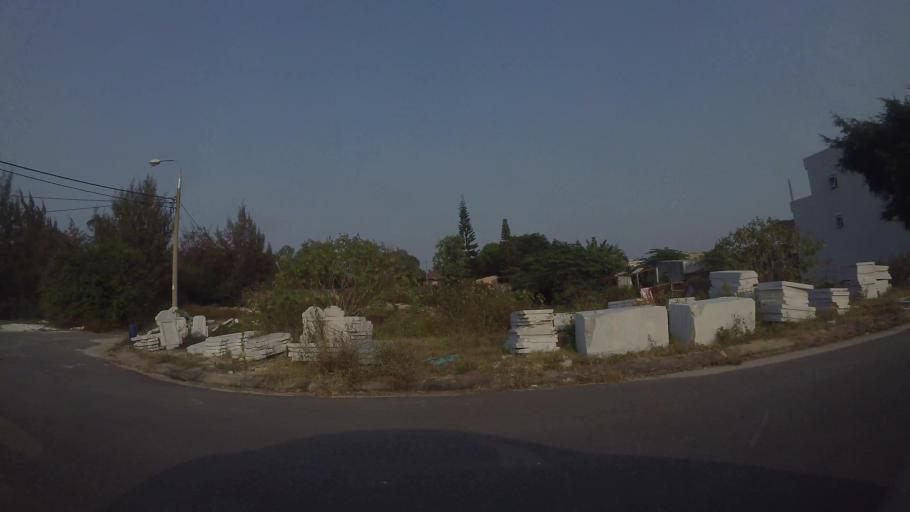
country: VN
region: Da Nang
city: Ngu Hanh Son
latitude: 15.9789
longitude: 108.2536
